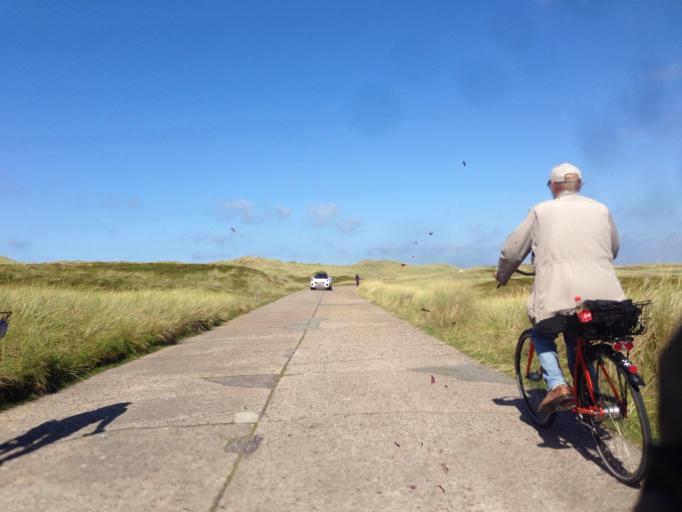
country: DE
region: Schleswig-Holstein
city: List
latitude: 55.0398
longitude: 8.3910
